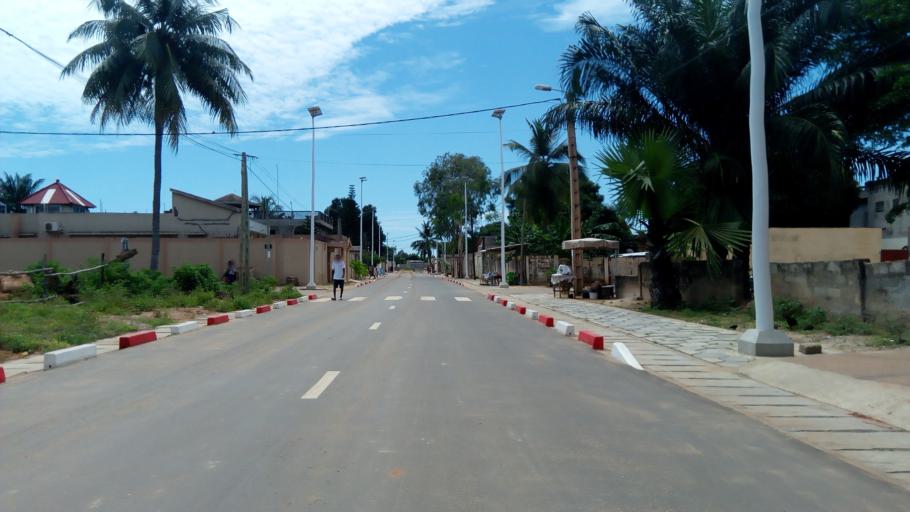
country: TG
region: Maritime
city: Lome
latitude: 6.1721
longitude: 1.1831
